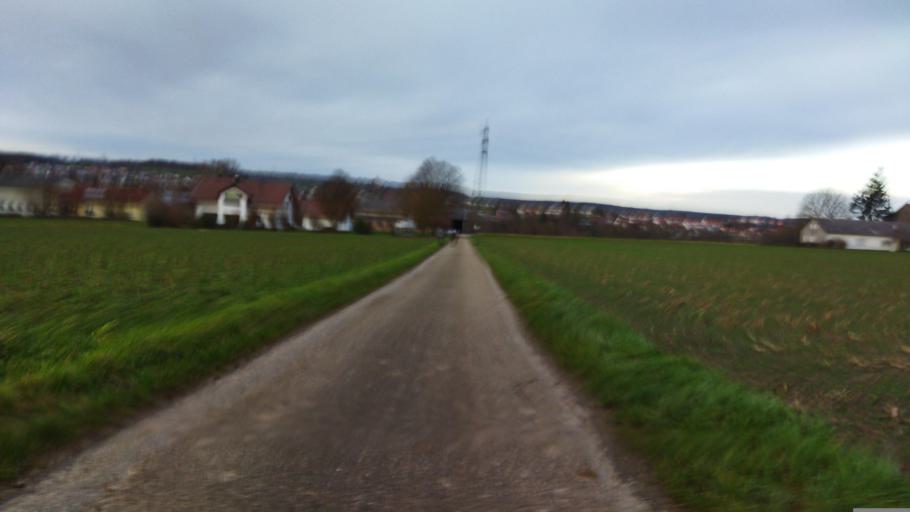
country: DE
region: Baden-Wuerttemberg
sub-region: Regierungsbezirk Stuttgart
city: Guglingen
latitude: 49.0590
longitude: 9.0103
